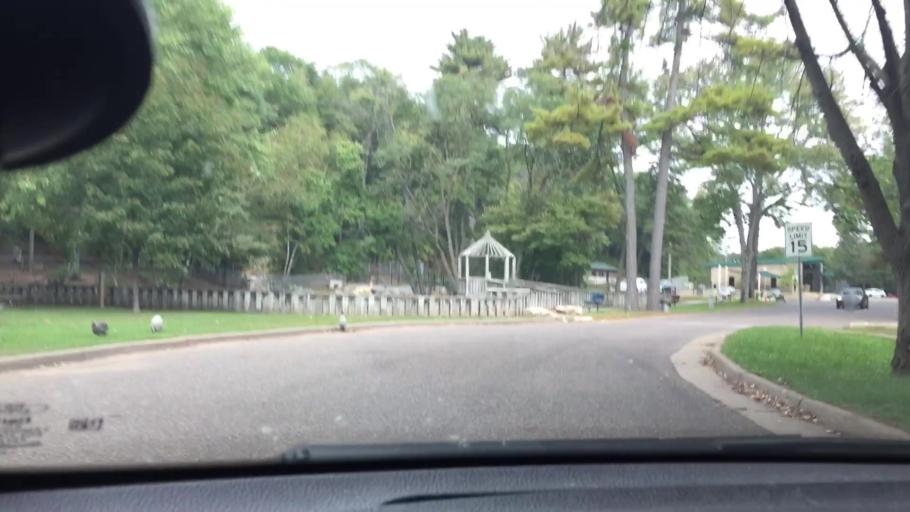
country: US
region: Wisconsin
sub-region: Chippewa County
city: Chippewa Falls
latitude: 44.9480
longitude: -91.4006
